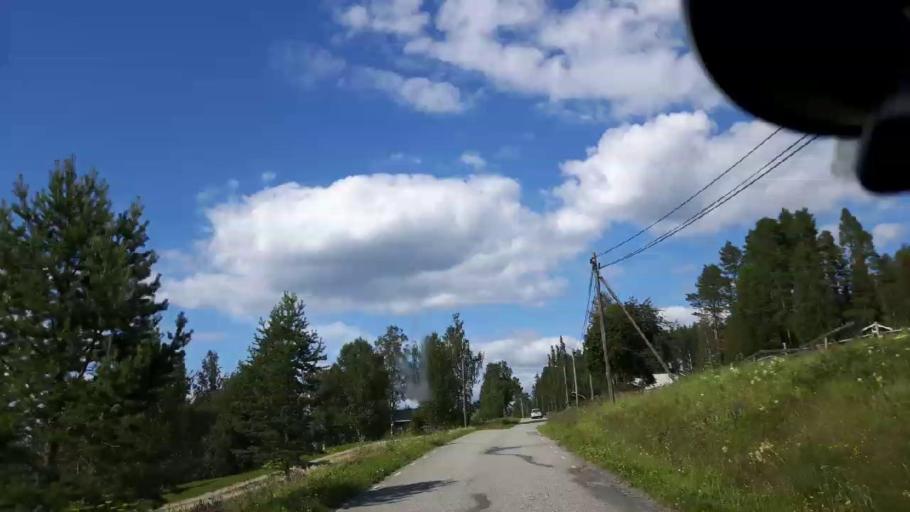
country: SE
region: Jaemtland
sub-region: Braecke Kommun
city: Braecke
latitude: 62.8686
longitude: 15.2719
